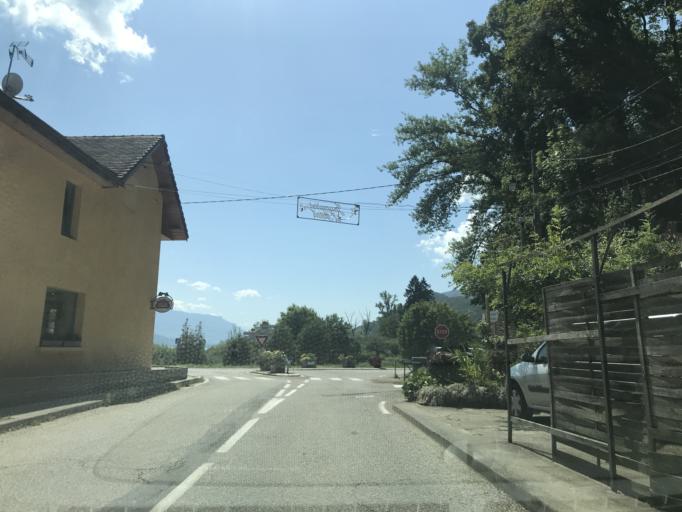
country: FR
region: Rhone-Alpes
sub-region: Departement de la Savoie
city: Chatillon
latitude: 45.8053
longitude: 5.8175
